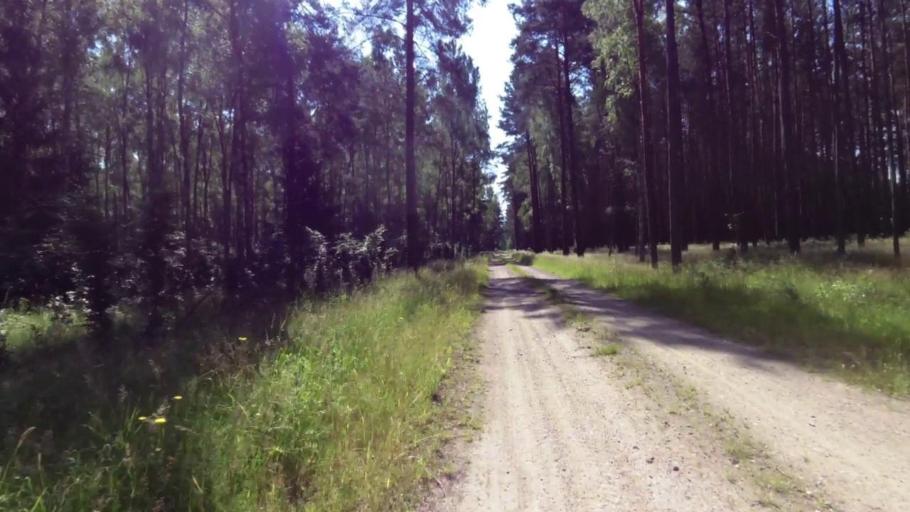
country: PL
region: West Pomeranian Voivodeship
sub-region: Powiat swidwinski
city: Polczyn-Zdroj
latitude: 53.8583
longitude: 16.1305
